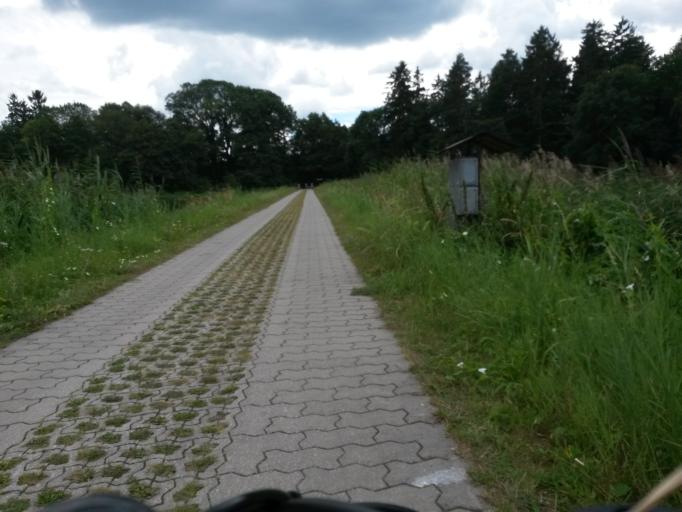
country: DE
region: Brandenburg
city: Angermunde
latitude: 53.0388
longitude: 13.9426
